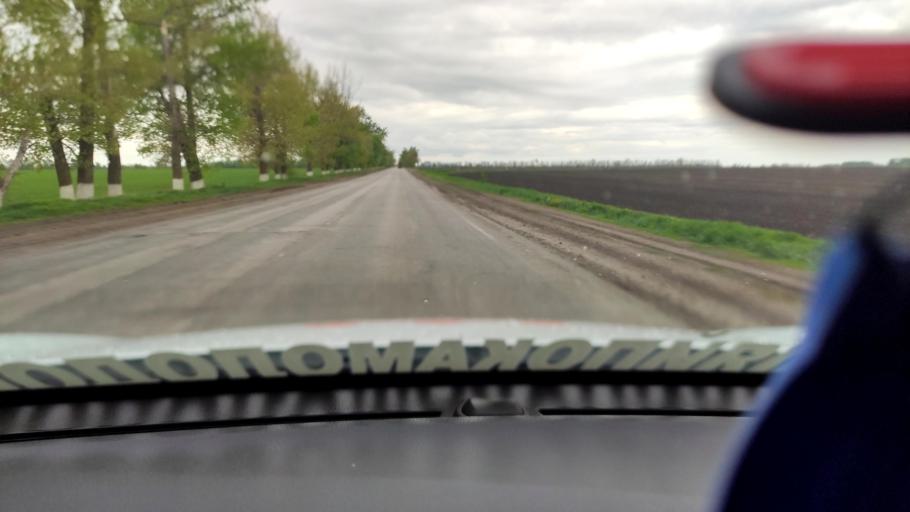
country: RU
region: Voronezj
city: Liski
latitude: 51.0299
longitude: 39.6087
